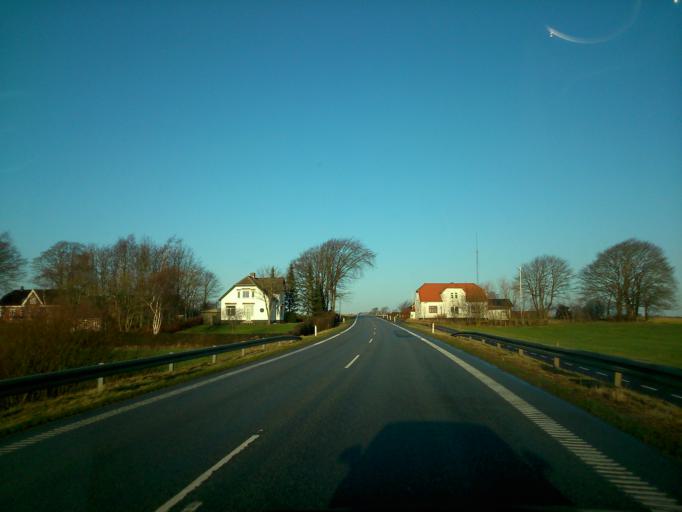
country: DK
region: Central Jutland
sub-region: Ringkobing-Skjern Kommune
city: Skjern
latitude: 55.9895
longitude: 8.5951
